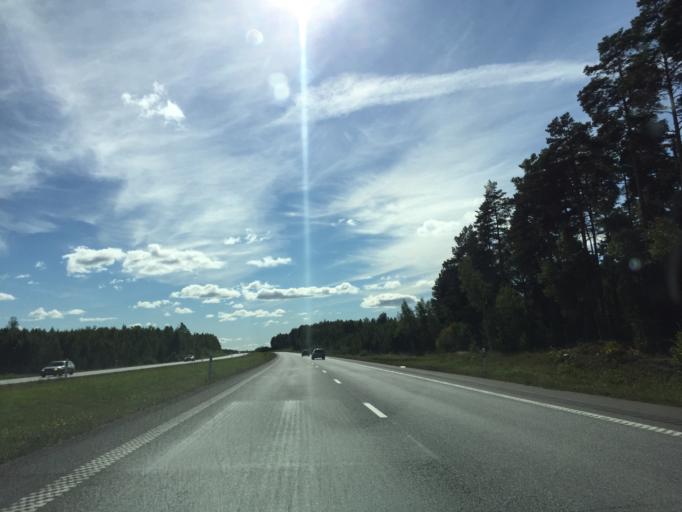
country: SE
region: Vaestmanland
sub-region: Arboga Kommun
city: Arboga
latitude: 59.4693
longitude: 15.9012
